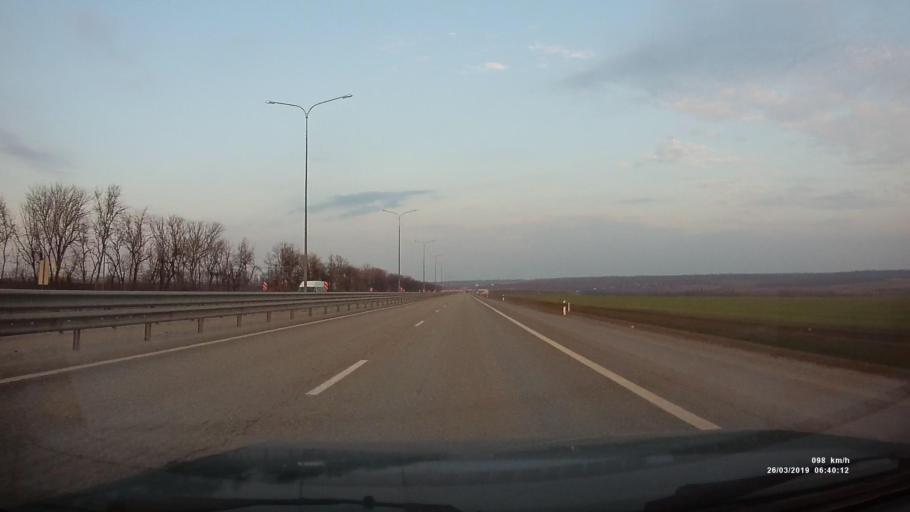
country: RU
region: Rostov
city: Sinyavskoye
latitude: 47.2878
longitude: 39.3480
